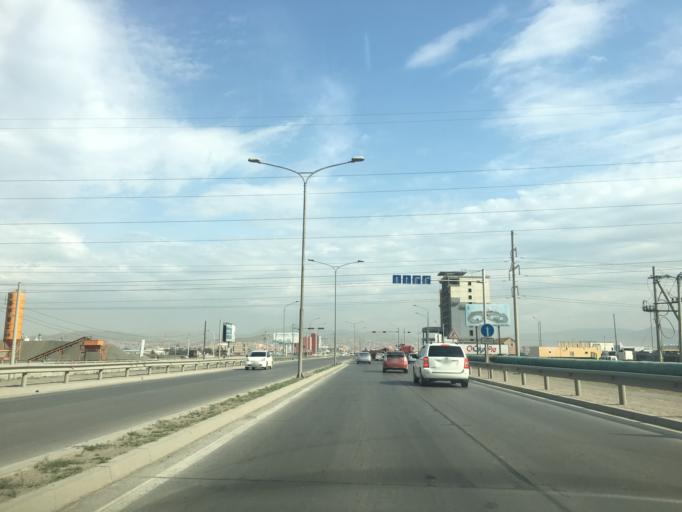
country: MN
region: Ulaanbaatar
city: Ulaanbaatar
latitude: 47.8891
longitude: 106.7853
